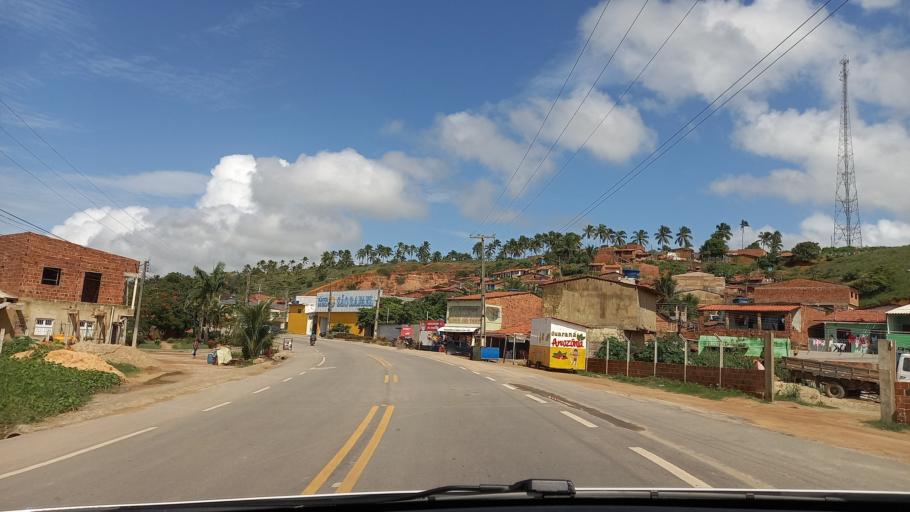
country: BR
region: Alagoas
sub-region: Maragogi
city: Maragogi
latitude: -8.9817
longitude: -35.1945
